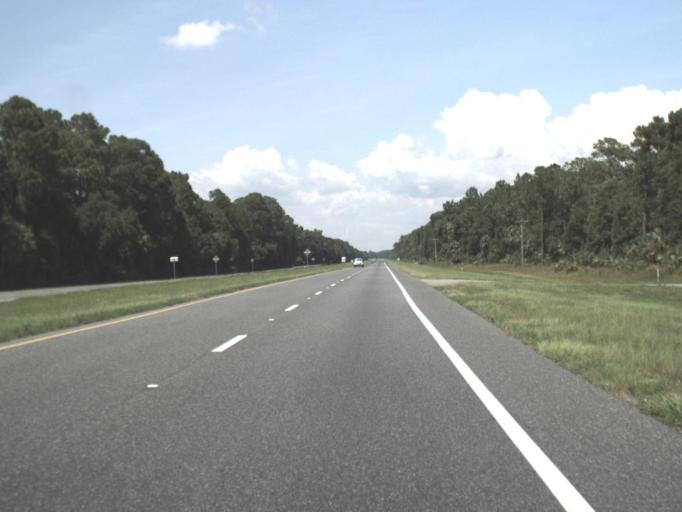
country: US
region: Florida
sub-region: Levy County
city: Inglis
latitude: 29.0441
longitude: -82.6656
